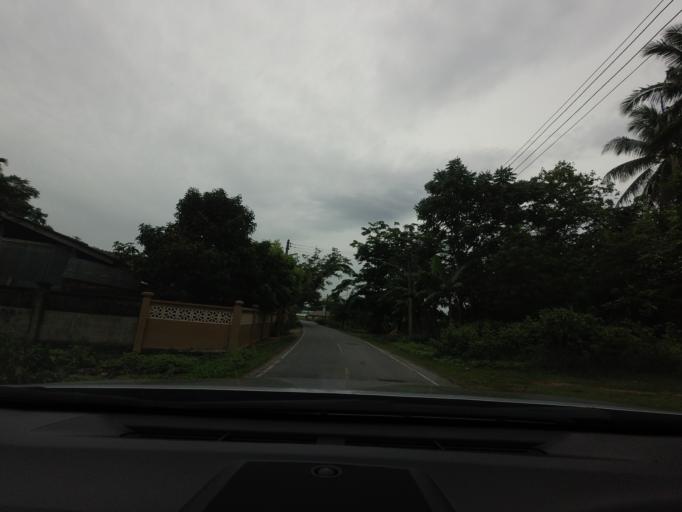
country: TH
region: Narathiwat
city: Rueso
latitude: 6.3990
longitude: 101.5152
